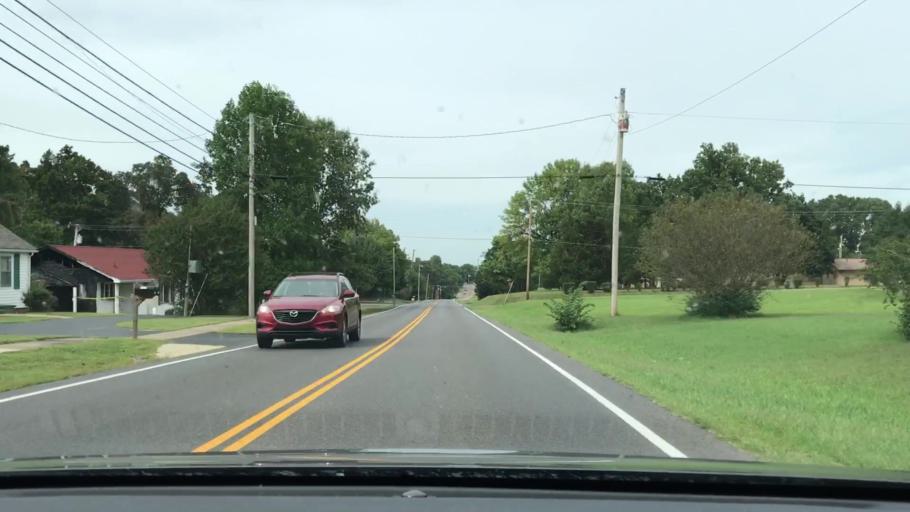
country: US
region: Kentucky
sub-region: Marshall County
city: Benton
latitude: 36.8470
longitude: -88.3499
